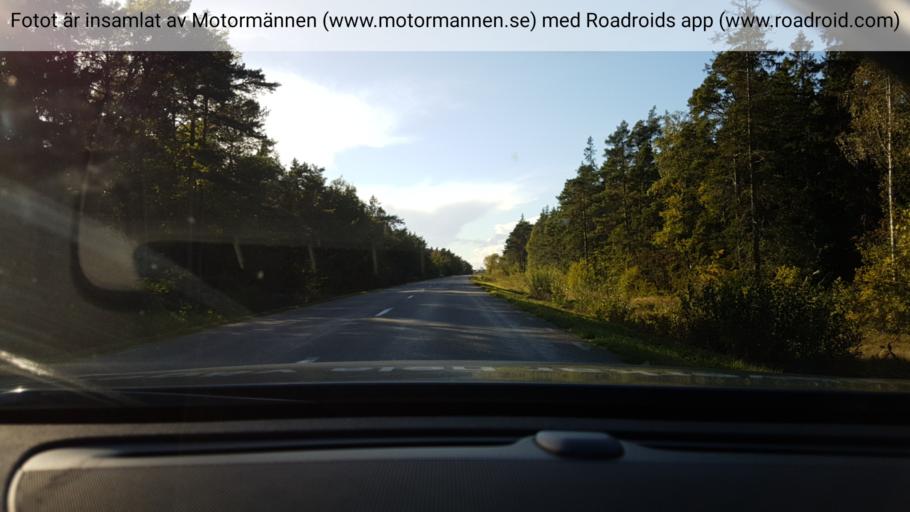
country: SE
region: Gotland
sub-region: Gotland
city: Klintehamn
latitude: 57.3799
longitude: 18.2121
